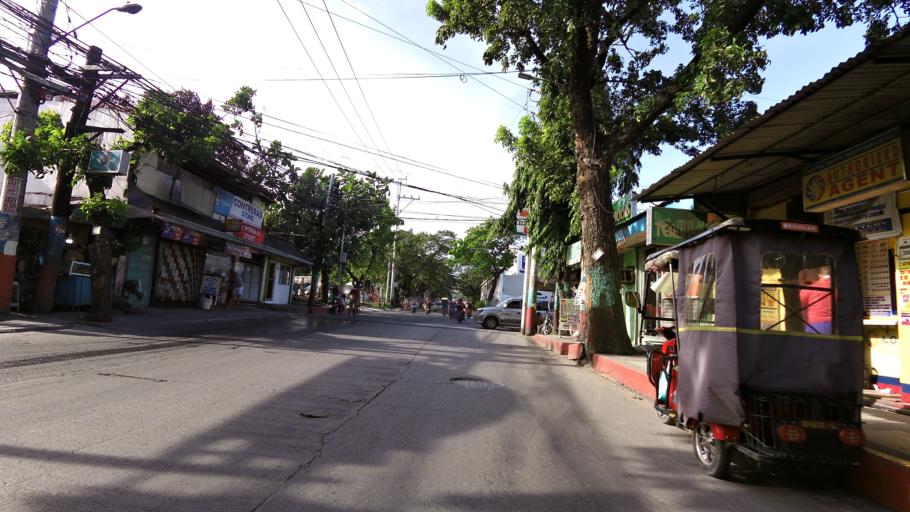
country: PH
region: Calabarzon
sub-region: Province of Rizal
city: Pateros
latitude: 14.5565
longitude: 121.0973
